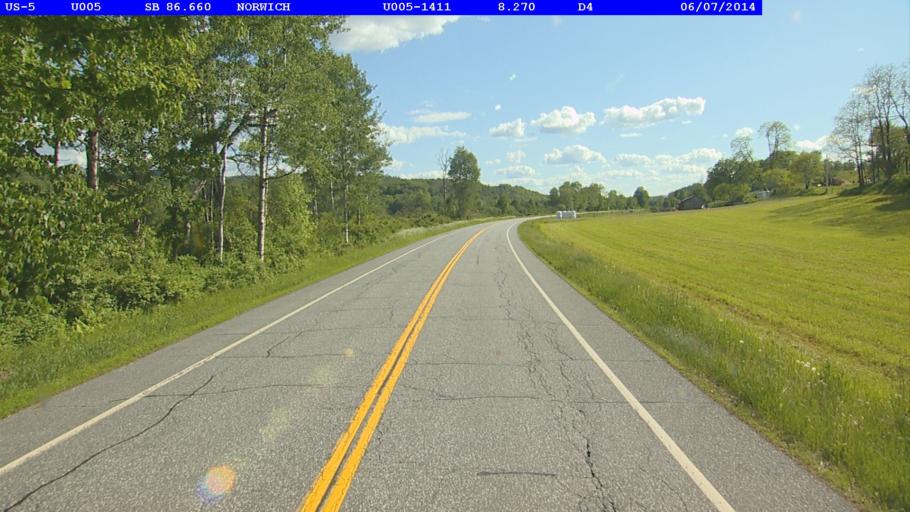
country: US
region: New Hampshire
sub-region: Grafton County
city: Lyme
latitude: 43.7717
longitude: -72.2074
